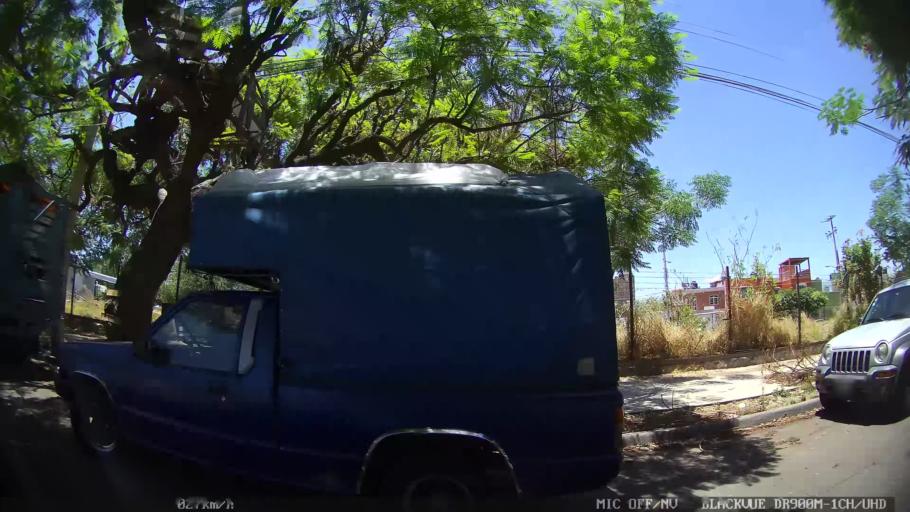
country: MX
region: Jalisco
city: Tlaquepaque
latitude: 20.6666
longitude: -103.2863
